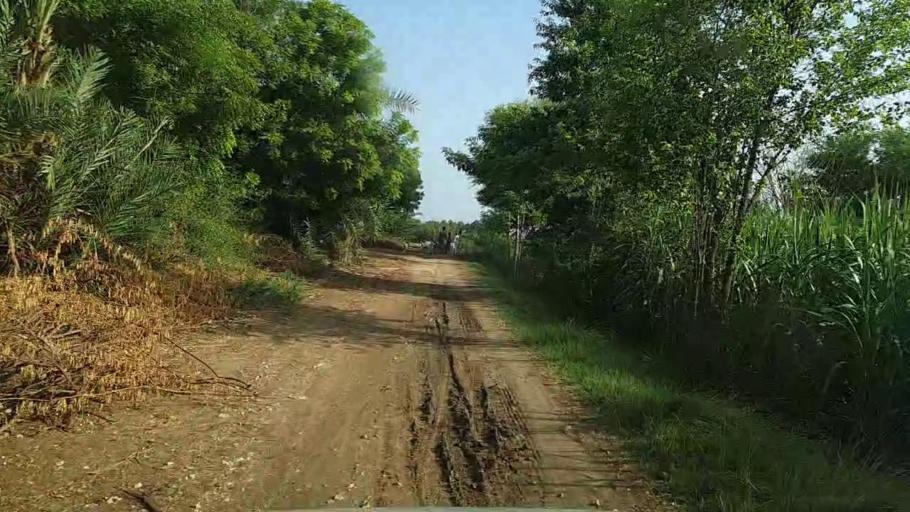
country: PK
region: Sindh
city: Pad Idan
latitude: 26.8354
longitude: 68.2410
